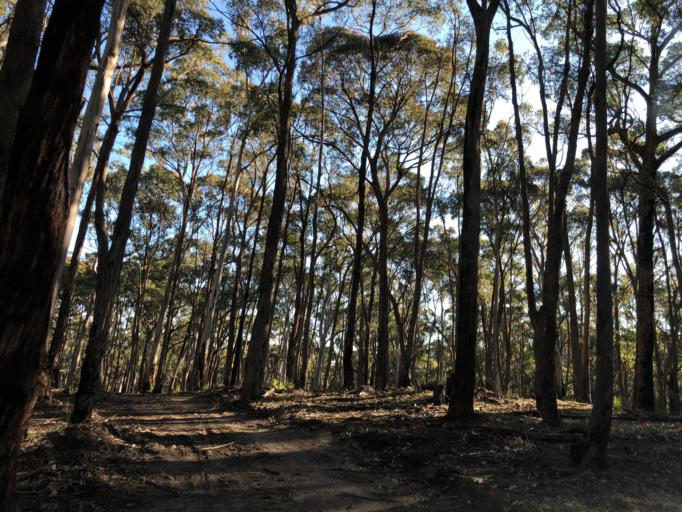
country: AU
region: Victoria
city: Brown Hill
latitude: -37.5107
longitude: 144.1817
